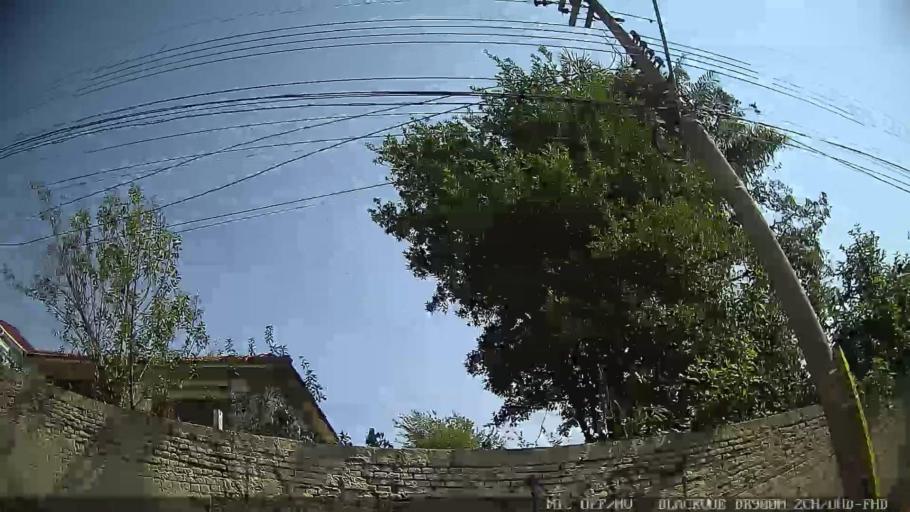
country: BR
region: Sao Paulo
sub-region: Itatiba
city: Itatiba
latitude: -23.0069
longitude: -46.8542
